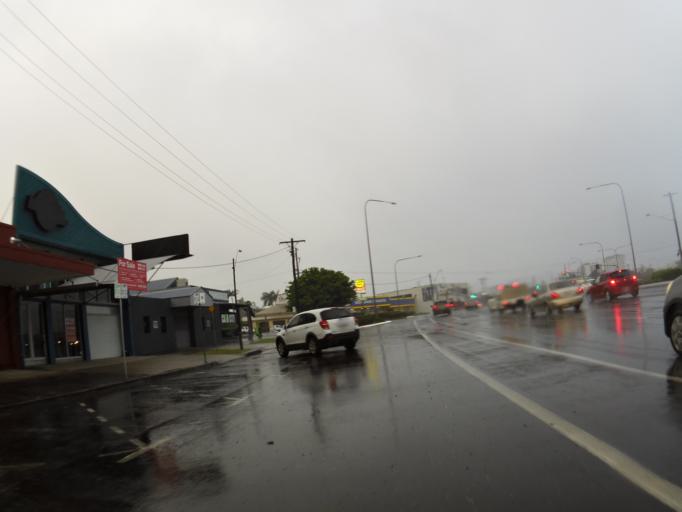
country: AU
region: Queensland
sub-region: Cairns
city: Cairns
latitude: -16.9240
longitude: 145.7654
